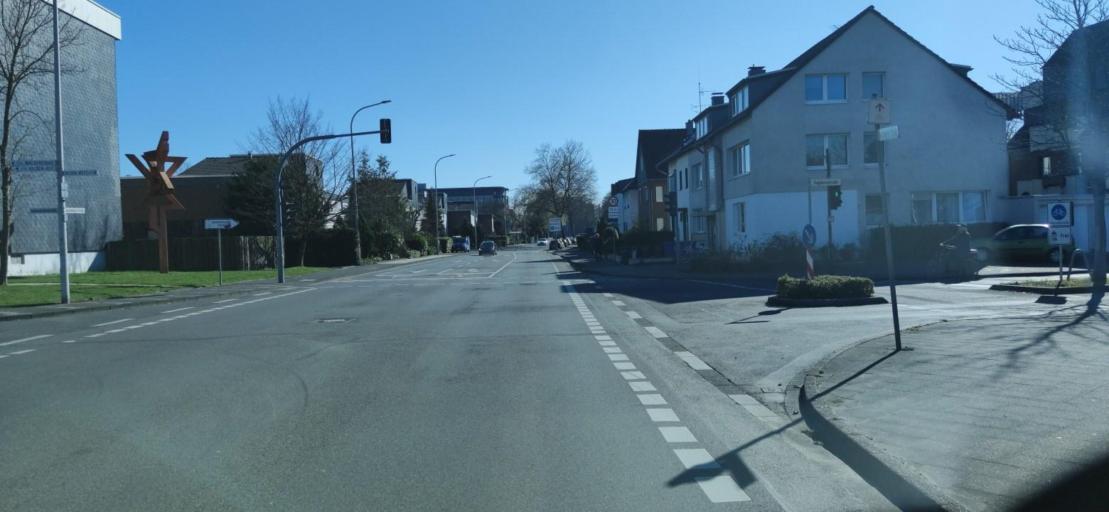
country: DE
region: North Rhine-Westphalia
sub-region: Regierungsbezirk Dusseldorf
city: Hilden
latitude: 51.1736
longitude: 6.9401
